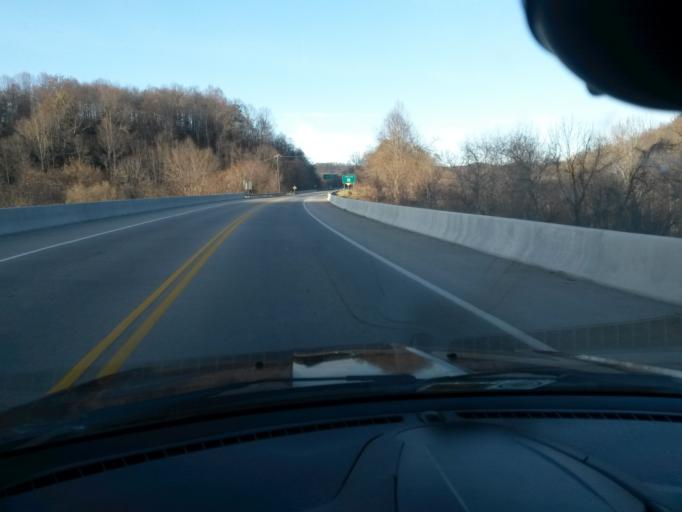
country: US
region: Virginia
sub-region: Alleghany County
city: Clifton Forge
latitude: 37.8141
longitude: -79.7993
